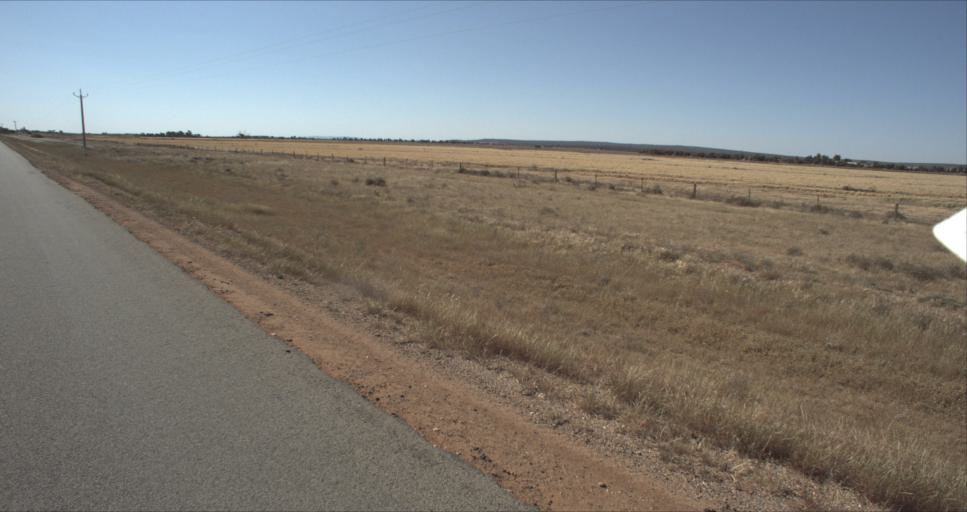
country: AU
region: New South Wales
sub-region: Leeton
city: Leeton
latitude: -34.4961
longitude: 146.3894
